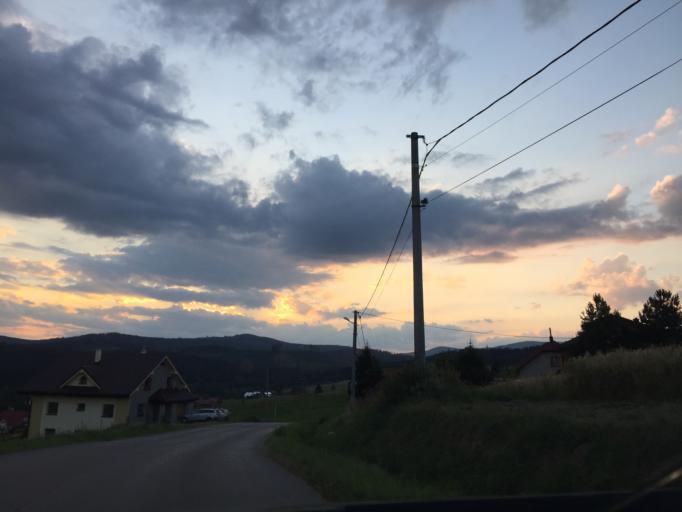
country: PL
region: Silesian Voivodeship
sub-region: Powiat zywiecki
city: Sopotnia Wielka
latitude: 49.4681
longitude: 19.3046
